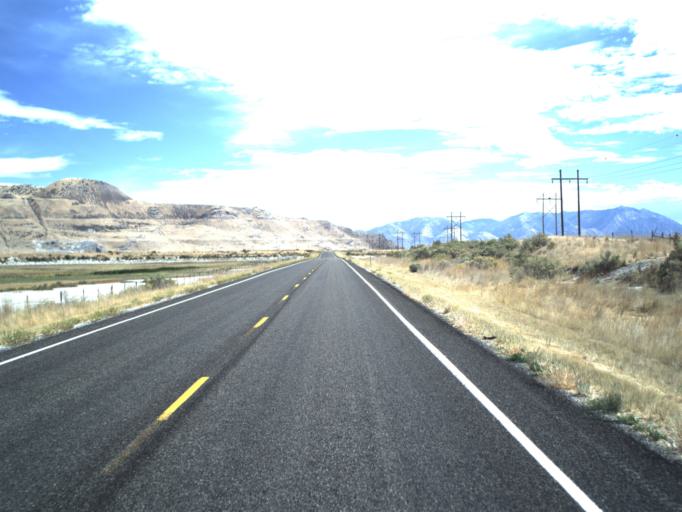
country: US
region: Utah
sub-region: Box Elder County
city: Tremonton
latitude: 41.6024
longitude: -112.3096
